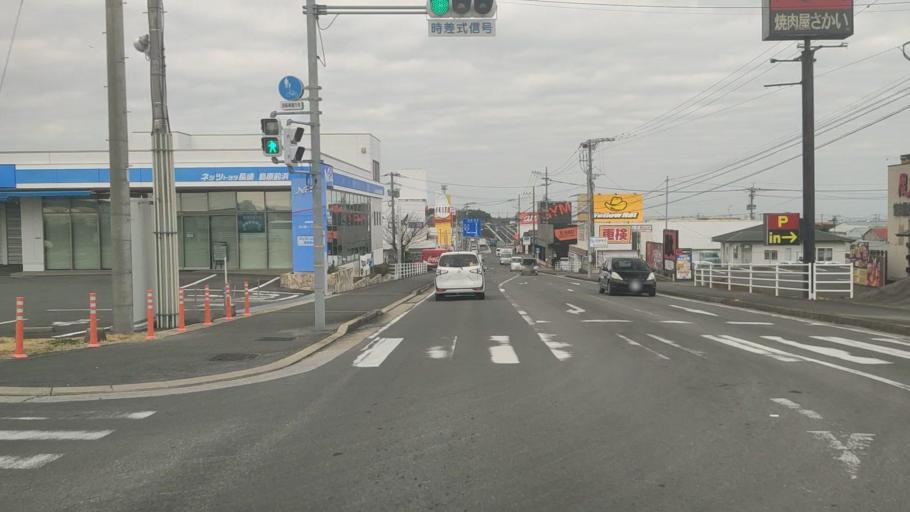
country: JP
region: Nagasaki
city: Shimabara
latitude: 32.8084
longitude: 130.3606
